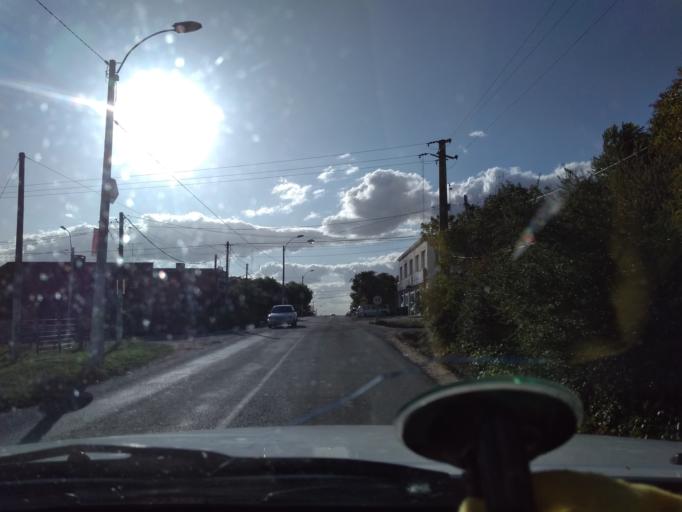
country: UY
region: Canelones
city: Tala
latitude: -34.3476
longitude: -55.7620
